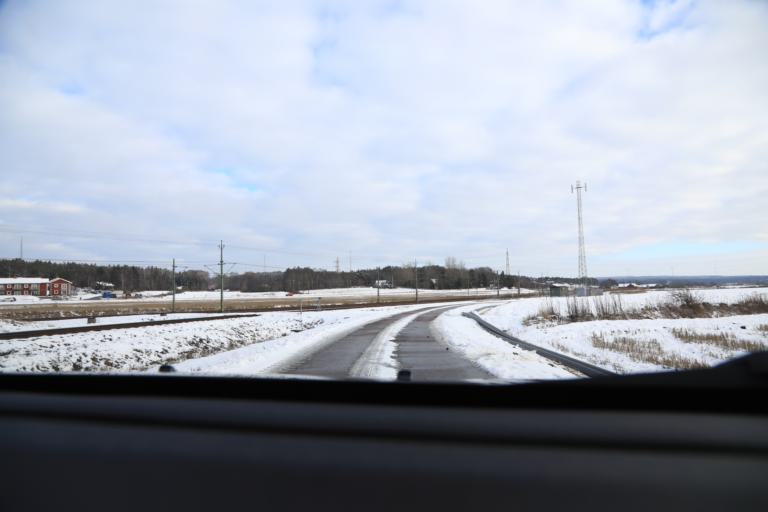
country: SE
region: Halland
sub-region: Kungsbacka Kommun
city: Frillesas
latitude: 57.2394
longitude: 12.1932
